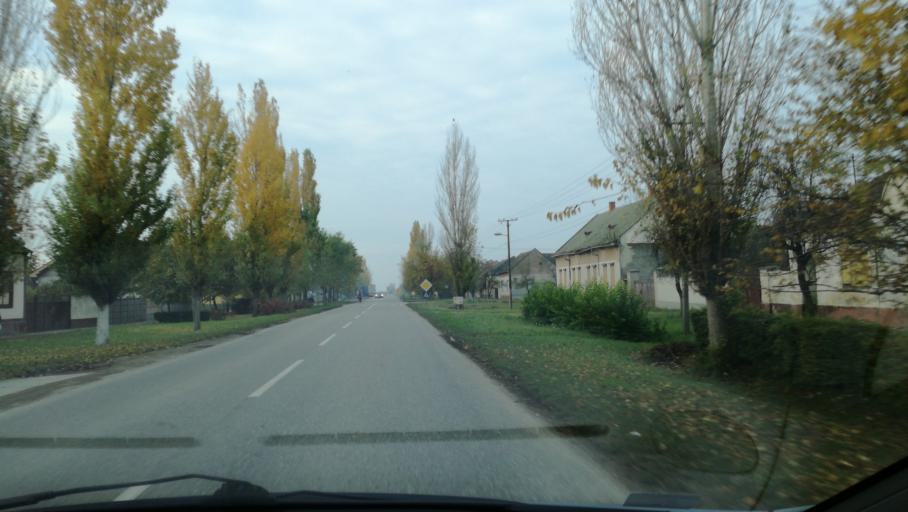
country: RS
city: Basaid
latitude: 45.6394
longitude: 20.4128
